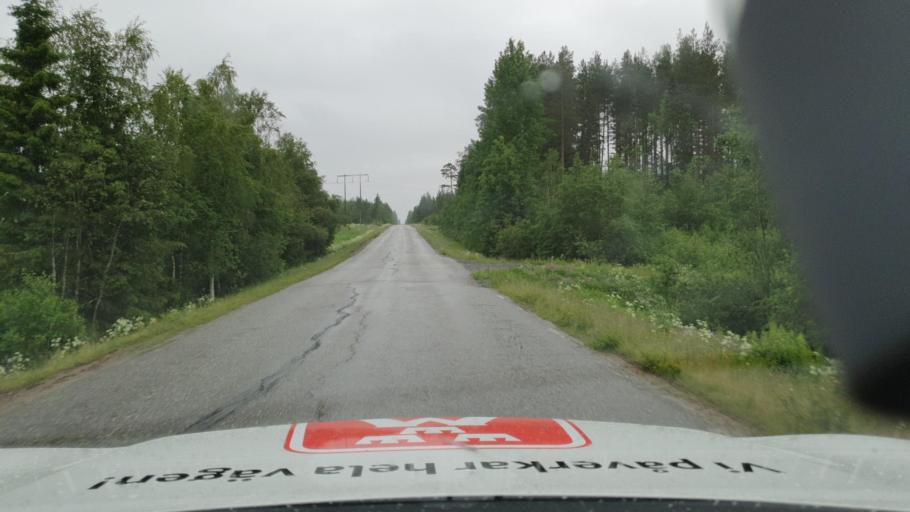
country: SE
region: Vaesterbotten
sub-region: Nordmalings Kommun
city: Nordmaling
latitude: 63.8121
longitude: 19.4994
